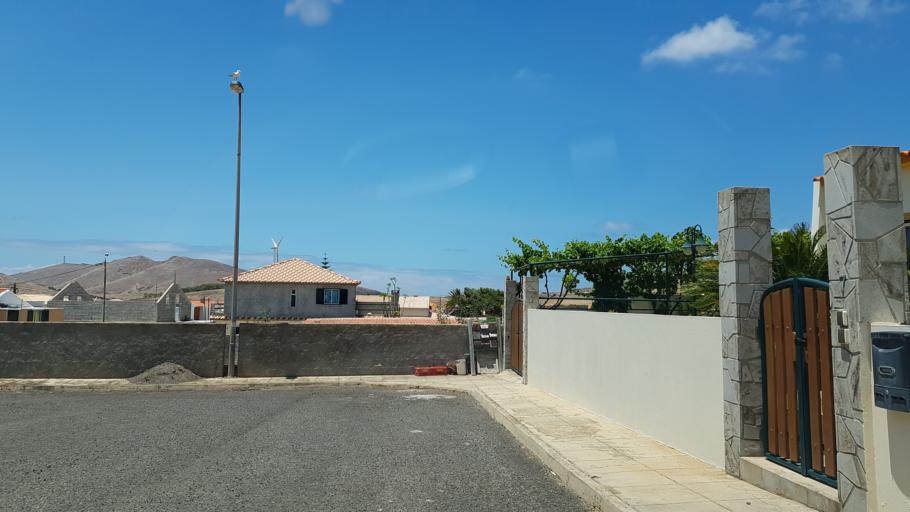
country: PT
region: Madeira
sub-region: Porto Santo
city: Vila de Porto Santo
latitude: 33.0630
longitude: -16.3548
